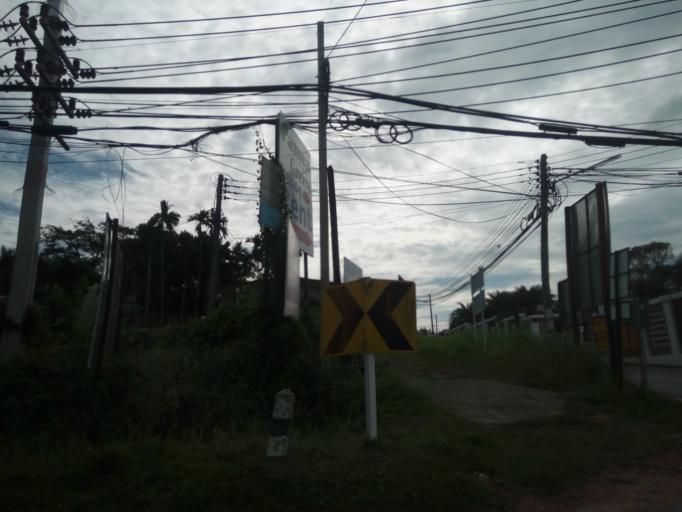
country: TH
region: Phuket
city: Mueang Phuket
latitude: 7.8437
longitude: 98.3857
